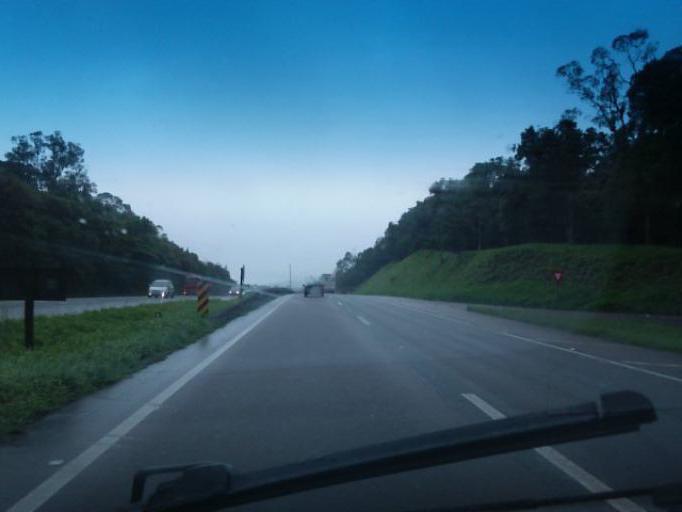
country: BR
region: Parana
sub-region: Sao Jose Dos Pinhais
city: Sao Jose dos Pinhais
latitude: -25.7877
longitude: -49.1235
